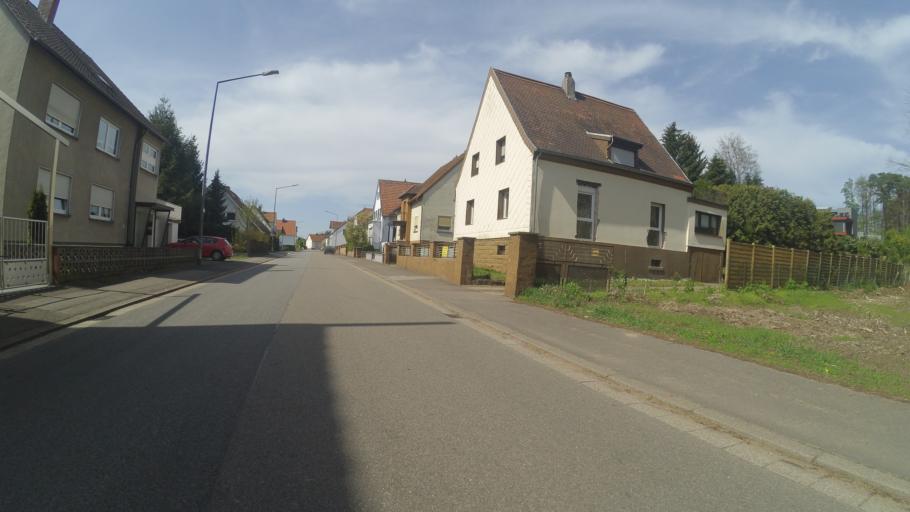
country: DE
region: Saarland
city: Homburg
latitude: 49.3424
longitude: 7.3614
